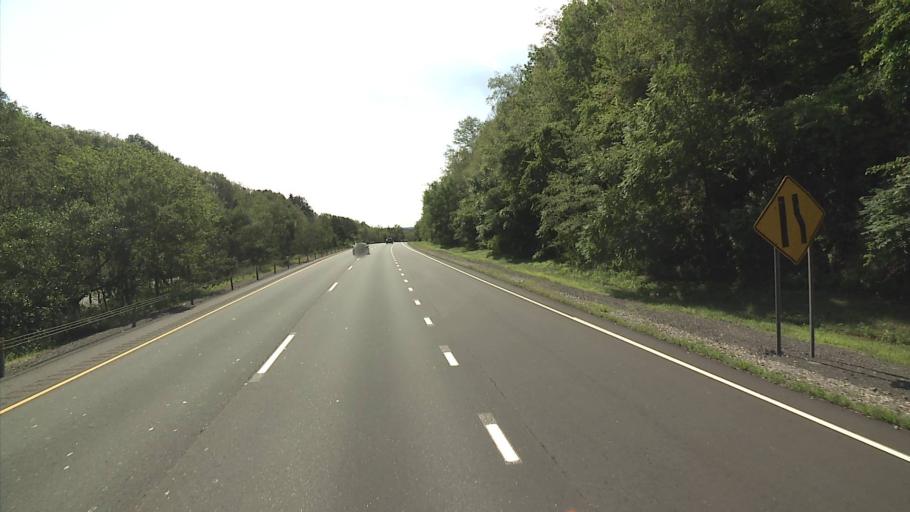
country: US
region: Connecticut
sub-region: Hartford County
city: Terramuggus
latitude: 41.6430
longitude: -72.4653
